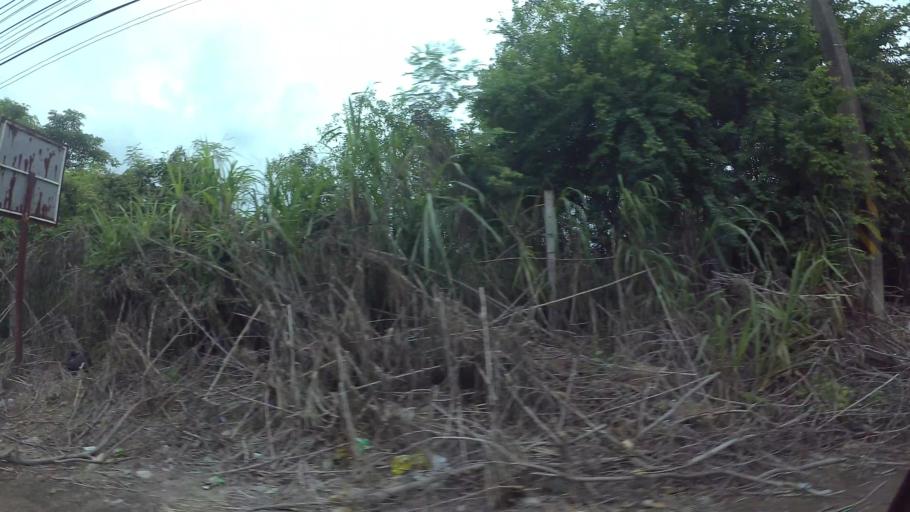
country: TH
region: Chon Buri
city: Si Racha
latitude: 13.1580
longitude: 100.9815
